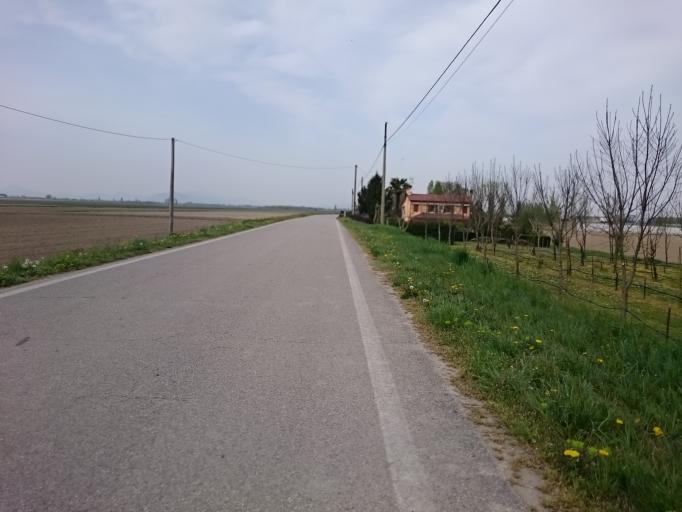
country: IT
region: Veneto
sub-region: Provincia di Padova
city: Anguillara Veneta
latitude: 45.1592
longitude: 11.8505
